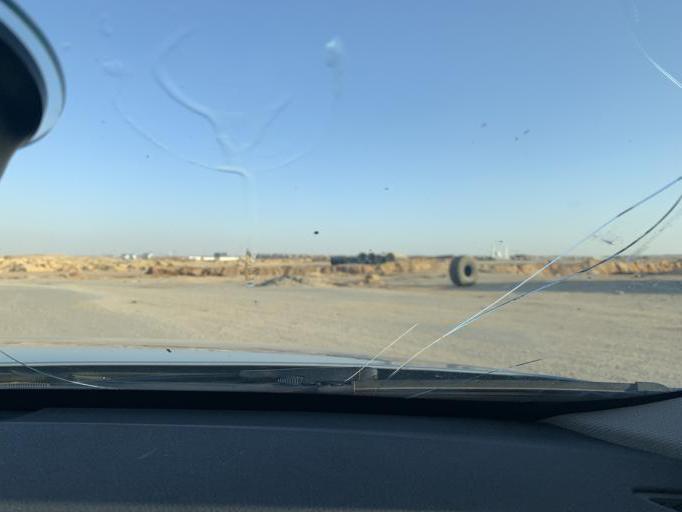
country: EG
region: Muhafazat al Qalyubiyah
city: Al Khankah
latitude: 30.0237
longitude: 31.6768
